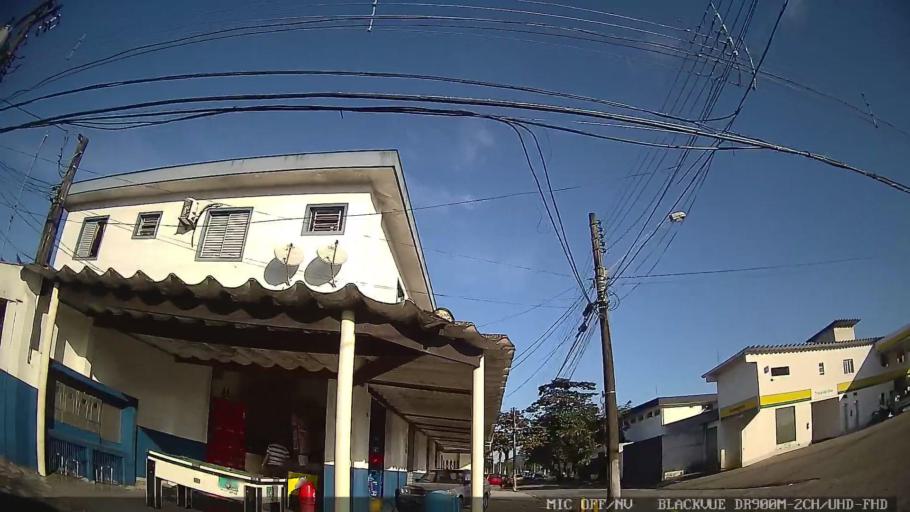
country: BR
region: Sao Paulo
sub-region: Guaruja
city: Guaruja
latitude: -23.9711
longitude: -46.2768
